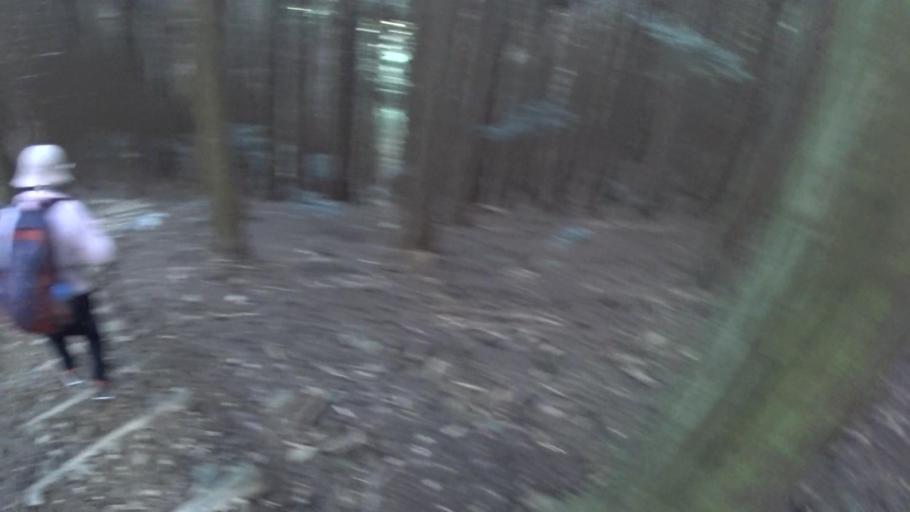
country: JP
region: Shiga Prefecture
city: Kitahama
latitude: 35.1022
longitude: 135.8433
